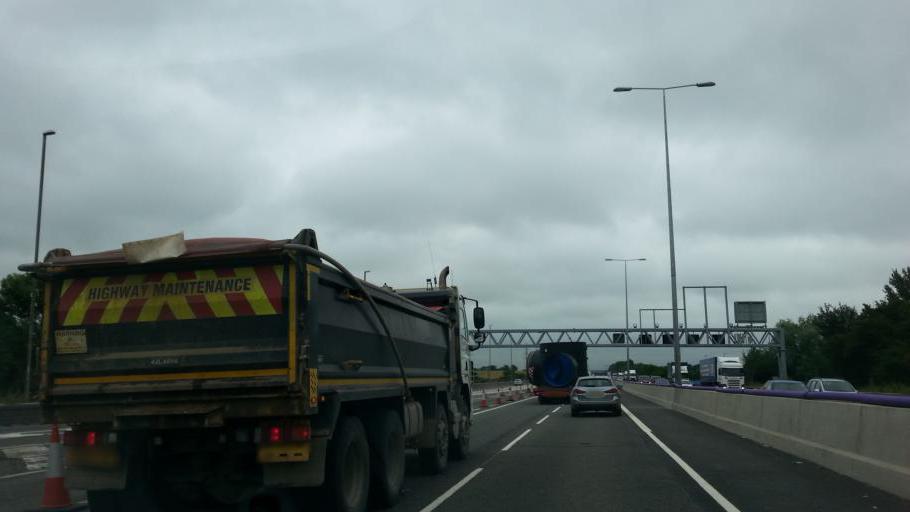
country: GB
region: England
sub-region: Leicestershire
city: Lutterworth
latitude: 52.3971
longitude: -1.1737
